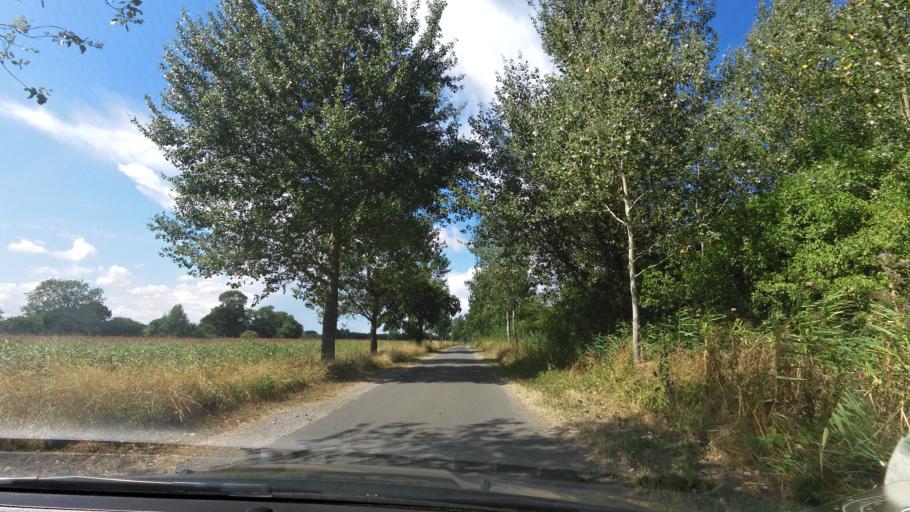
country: DK
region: South Denmark
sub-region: Nordfyns Kommune
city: Otterup
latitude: 55.5433
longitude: 10.4699
